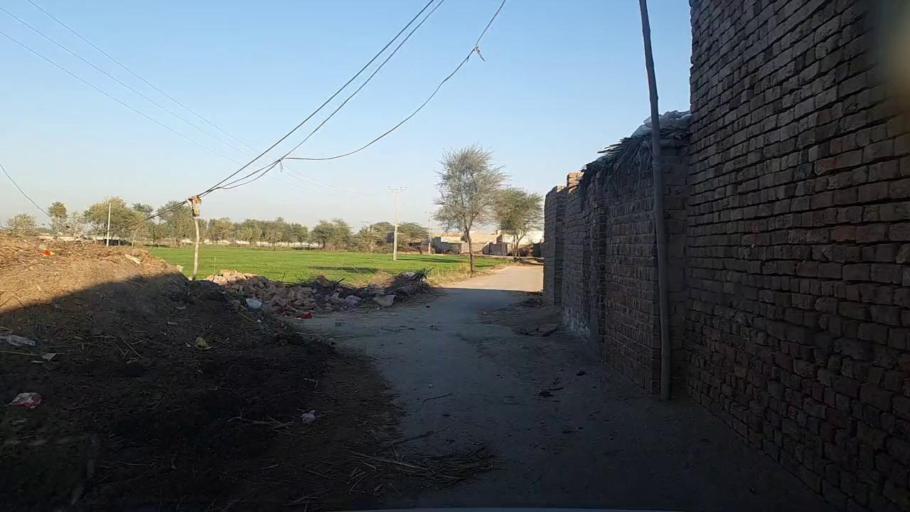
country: PK
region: Sindh
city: Khairpur
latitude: 28.0430
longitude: 69.7100
